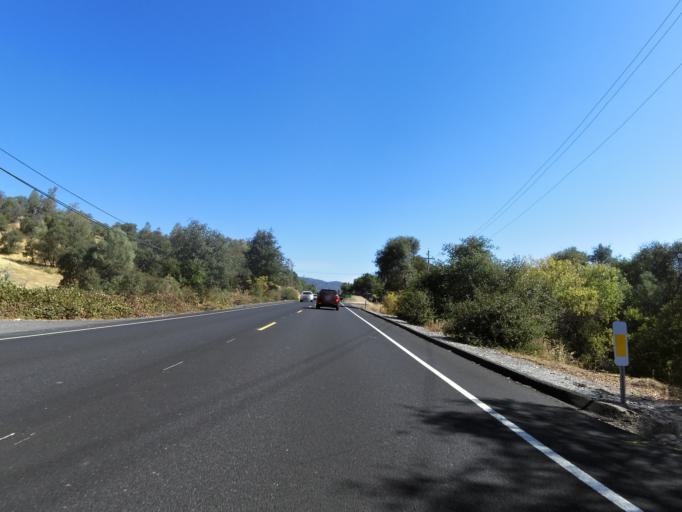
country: US
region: California
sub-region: Calaveras County
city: Murphys
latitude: 38.1088
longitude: -120.4614
